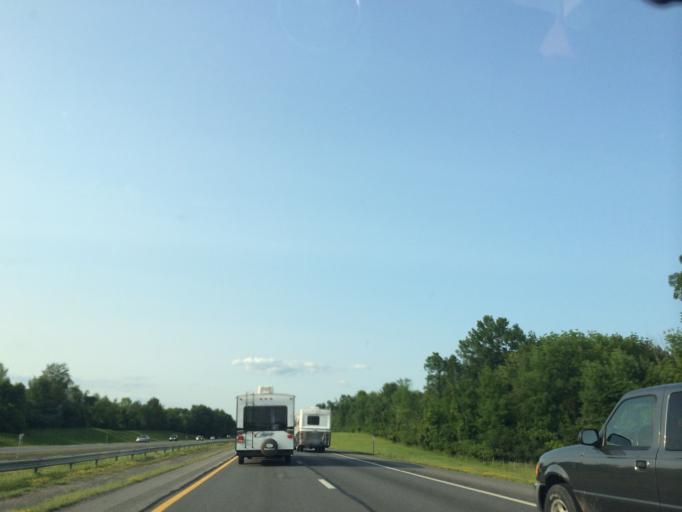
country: US
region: New York
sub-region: Albany County
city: Ravena
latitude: 42.4565
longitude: -73.8099
